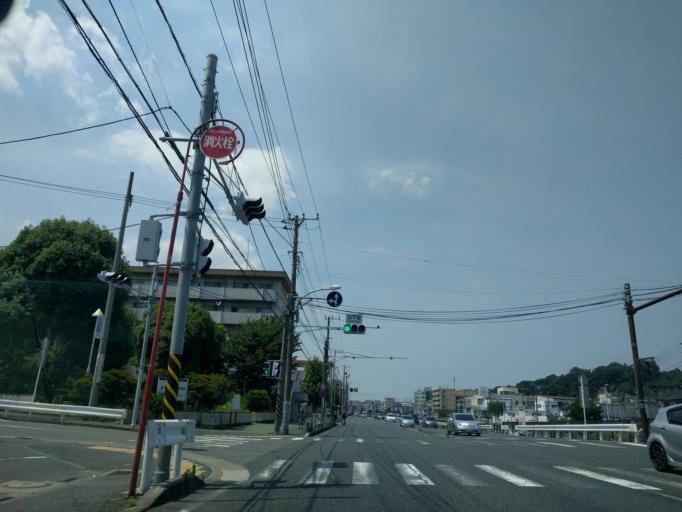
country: JP
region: Kanagawa
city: Yokohama
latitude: 35.4189
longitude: 139.6259
